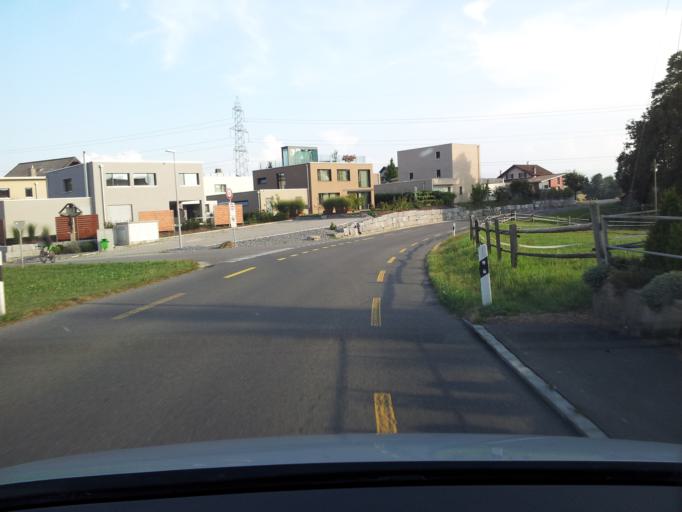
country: CH
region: Lucerne
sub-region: Sursee District
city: Eich
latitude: 47.1715
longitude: 8.1683
